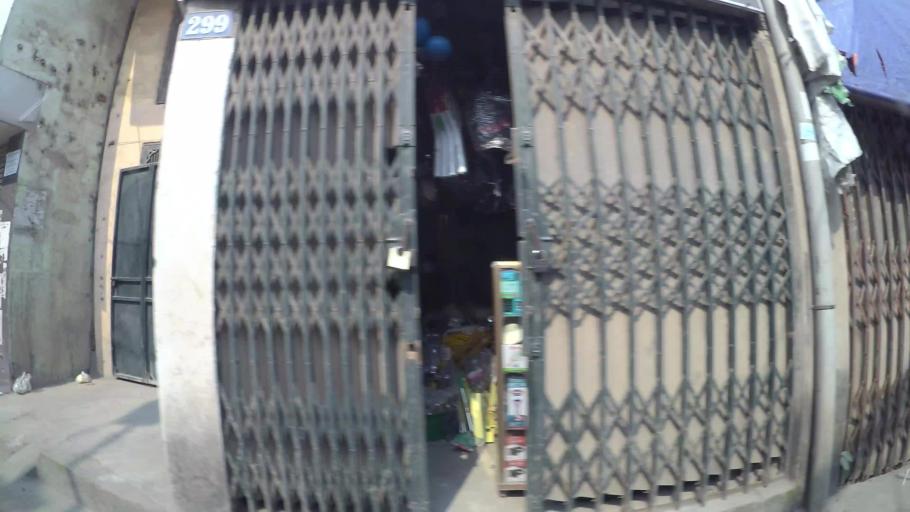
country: VN
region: Ha Noi
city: Thanh Xuan
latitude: 20.9844
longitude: 105.8198
